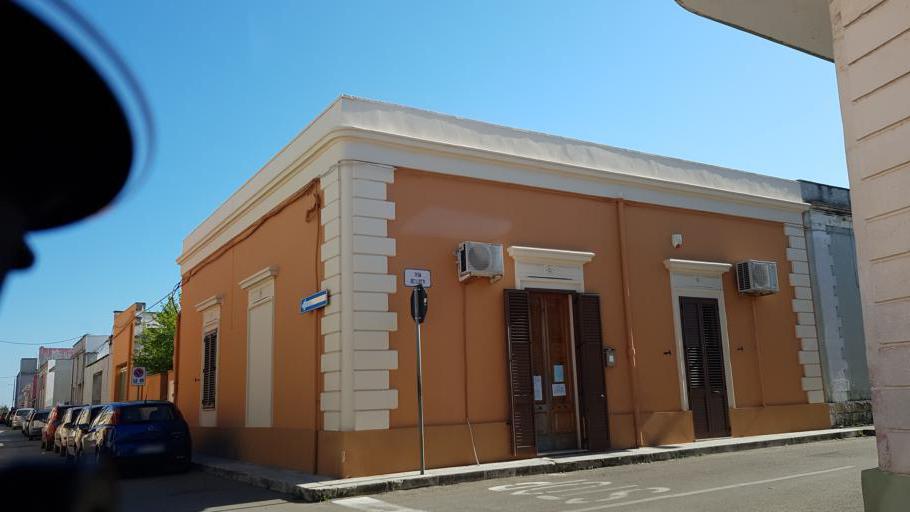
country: IT
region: Apulia
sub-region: Provincia di Brindisi
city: Torchiarolo
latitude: 40.4841
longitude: 18.0554
